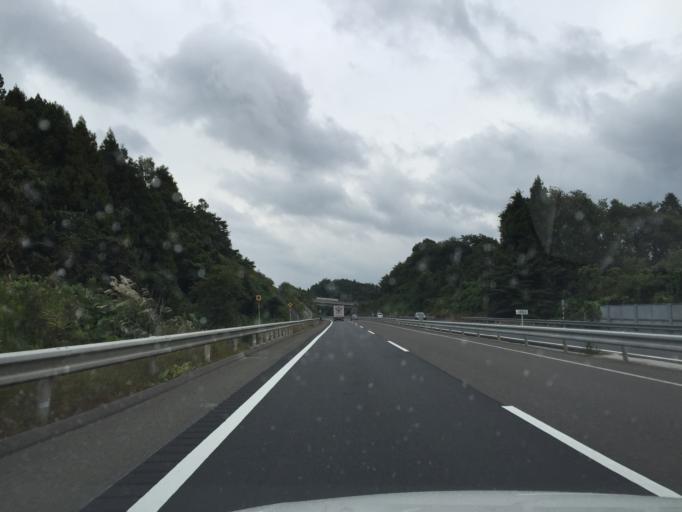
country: JP
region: Fukushima
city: Funehikimachi-funehiki
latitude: 37.4035
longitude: 140.5704
